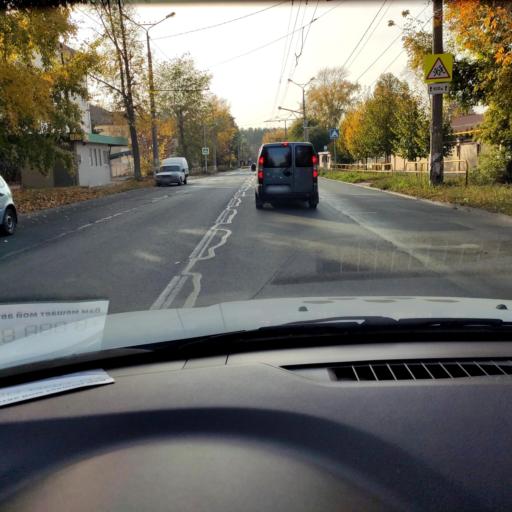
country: RU
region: Samara
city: Tol'yatti
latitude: 53.5061
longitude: 49.3969
